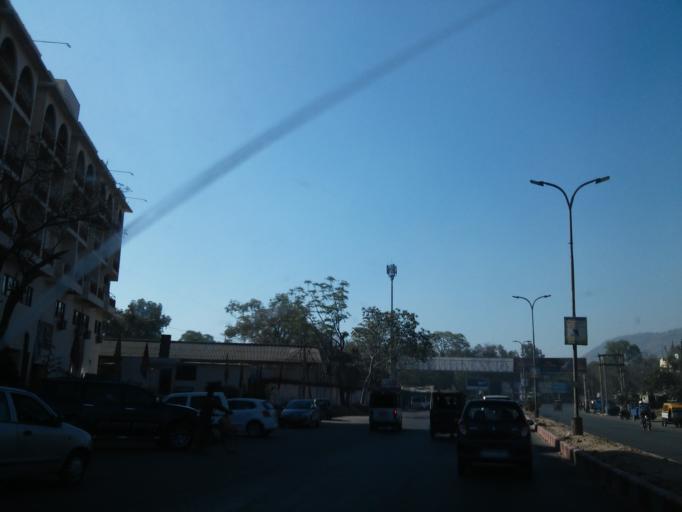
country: IN
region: Rajasthan
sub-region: Udaipur
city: Udaipur
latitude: 24.5685
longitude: 73.6989
